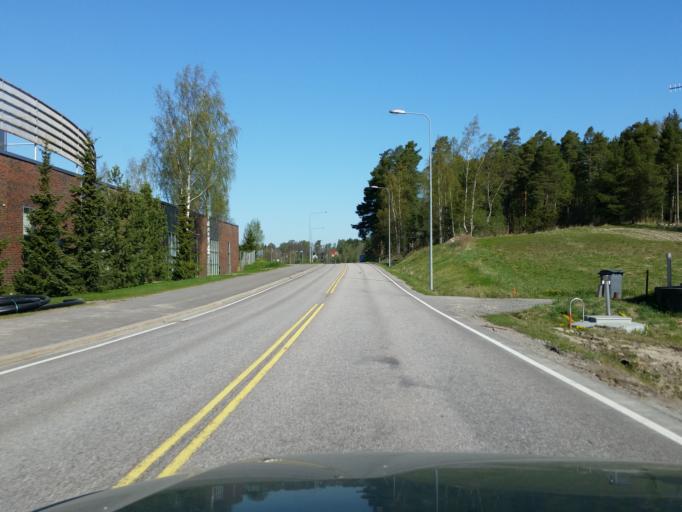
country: FI
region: Uusimaa
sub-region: Helsinki
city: Kirkkonummi
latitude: 60.1307
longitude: 24.5157
